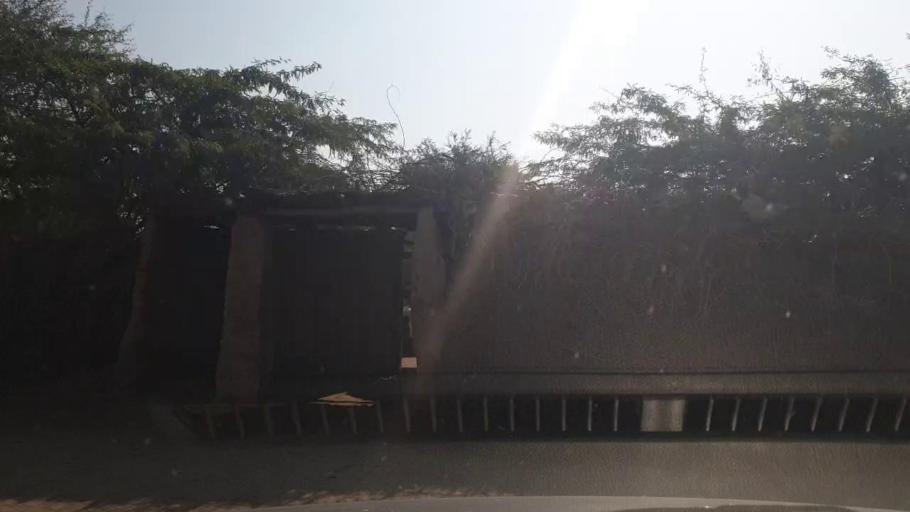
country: PK
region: Sindh
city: Tando Adam
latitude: 25.7460
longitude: 68.5897
